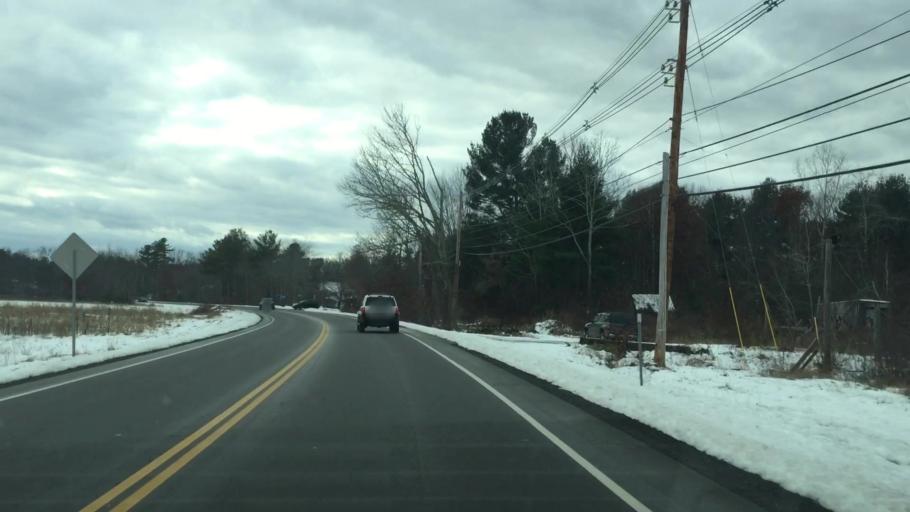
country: US
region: New Hampshire
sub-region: Hillsborough County
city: Pelham
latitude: 42.7441
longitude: -71.2958
